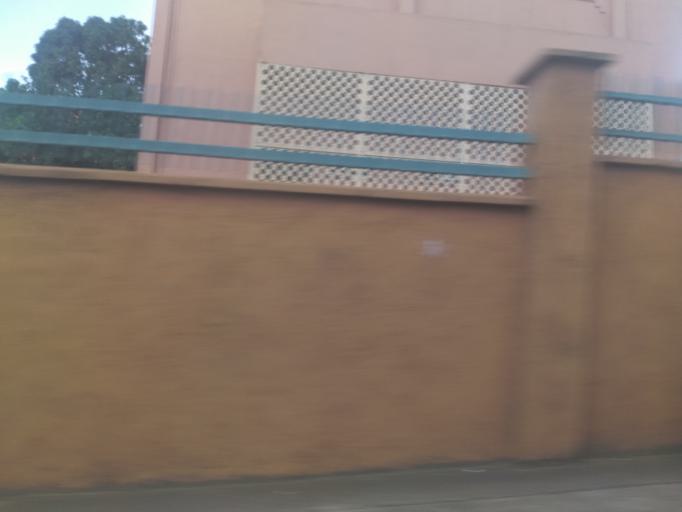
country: UG
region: Central Region
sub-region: Kampala District
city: Kampala
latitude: 0.3200
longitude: 32.5868
